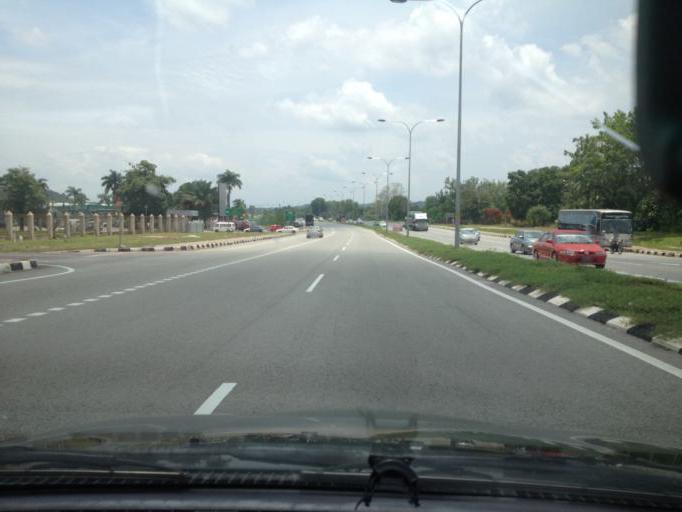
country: MY
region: Kedah
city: Sungai Petani
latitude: 5.6238
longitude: 100.5354
